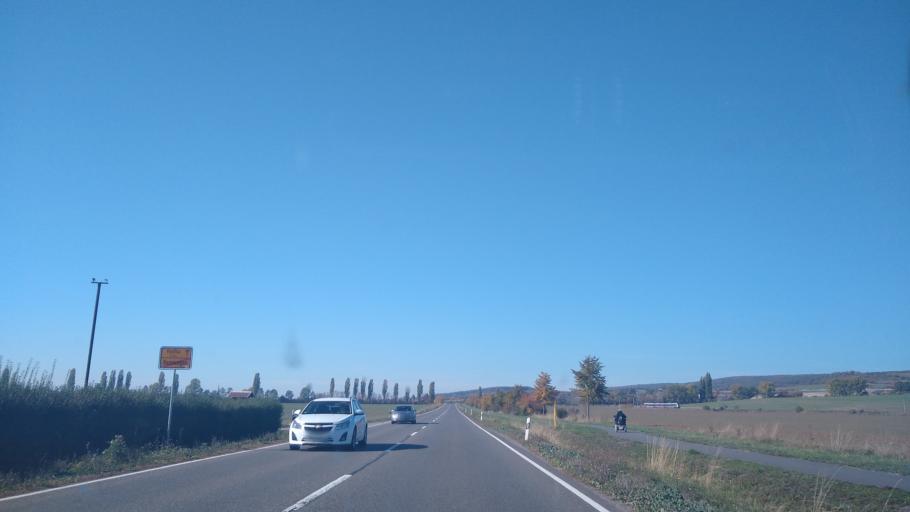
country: DE
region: Saxony-Anhalt
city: Bennungen
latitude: 51.4631
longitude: 11.1103
